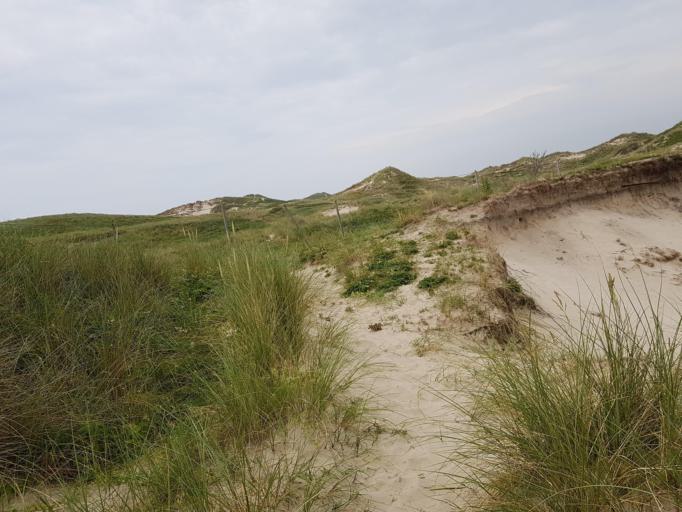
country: NL
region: North Holland
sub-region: Gemeente Bergen
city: Egmond aan Zee
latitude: 52.6312
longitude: 4.6253
